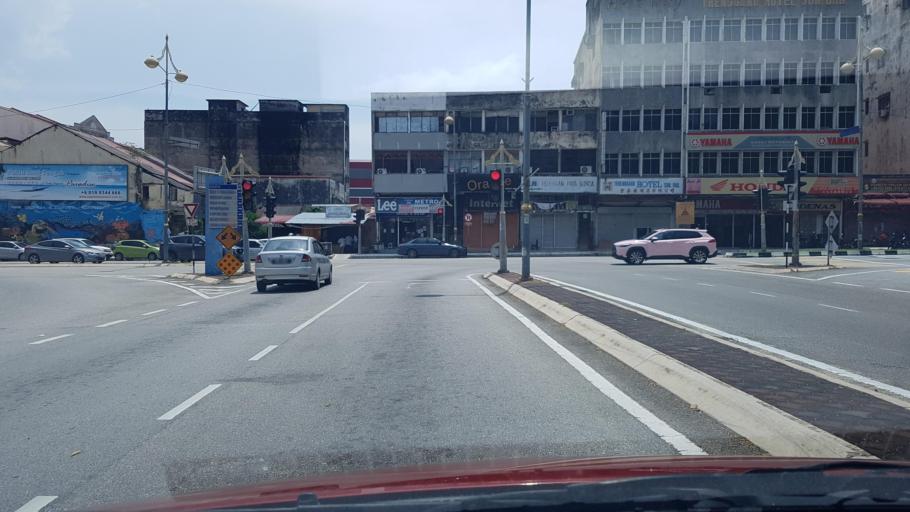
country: MY
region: Terengganu
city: Kuala Terengganu
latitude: 5.3305
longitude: 103.1328
